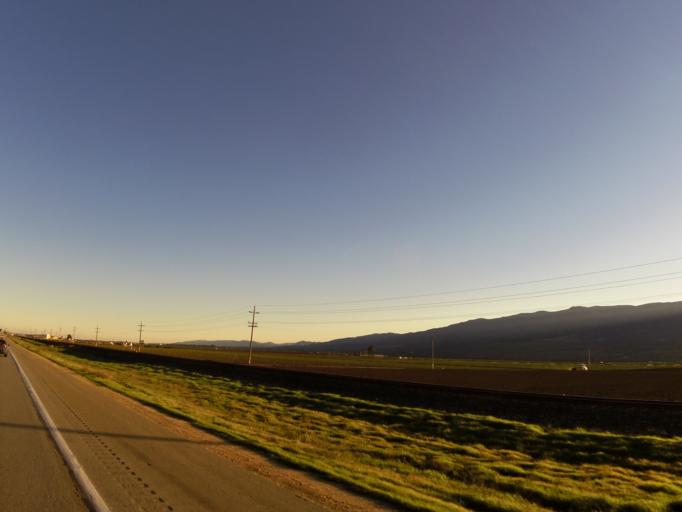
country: US
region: California
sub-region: Monterey County
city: Gonzales
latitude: 36.4740
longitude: -121.4026
